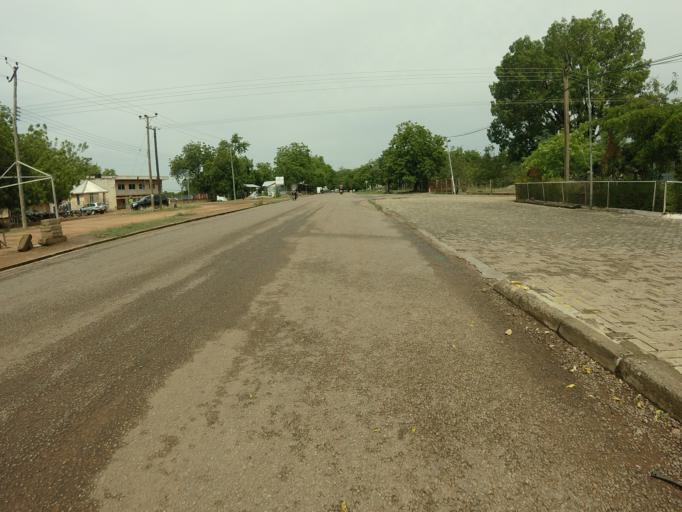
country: GH
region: Upper East
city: Bolgatanga
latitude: 10.7961
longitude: -0.8575
